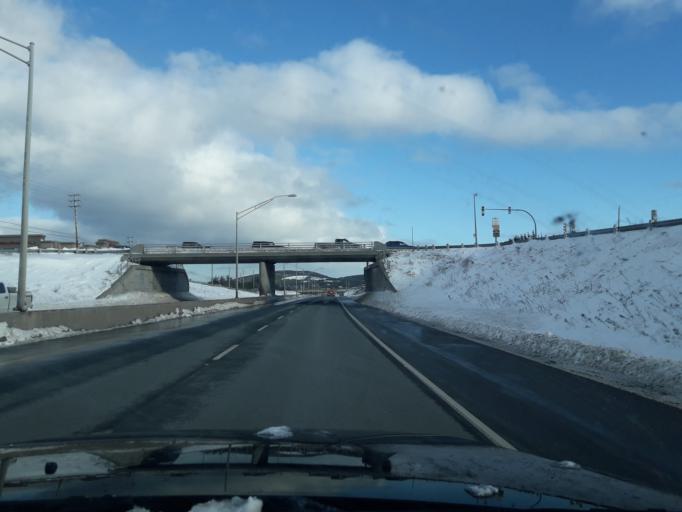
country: CA
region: Newfoundland and Labrador
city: St. John's
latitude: 47.6129
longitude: -52.7126
